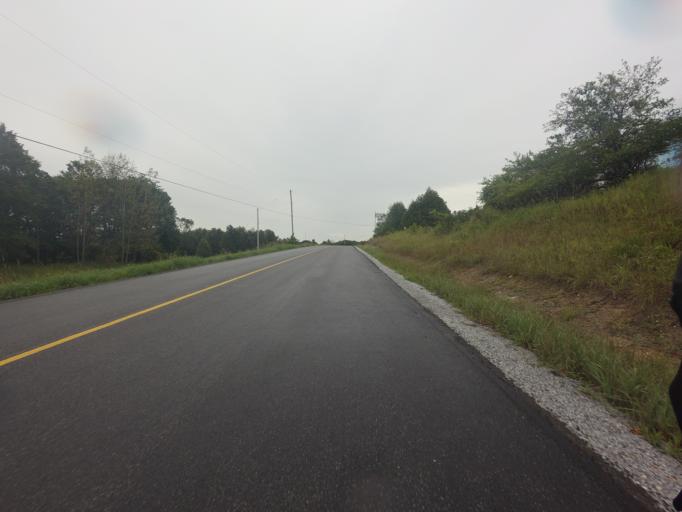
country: CA
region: Ontario
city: Perth
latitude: 44.9229
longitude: -76.4658
